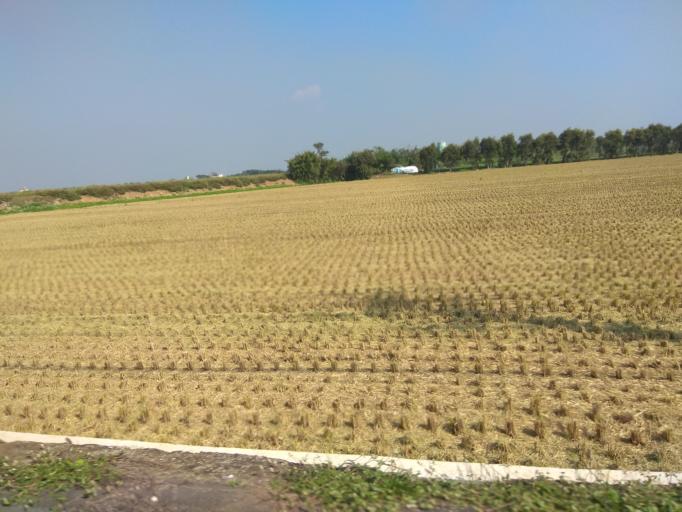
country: TW
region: Taiwan
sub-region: Hsinchu
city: Zhubei
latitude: 24.9913
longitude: 121.0703
